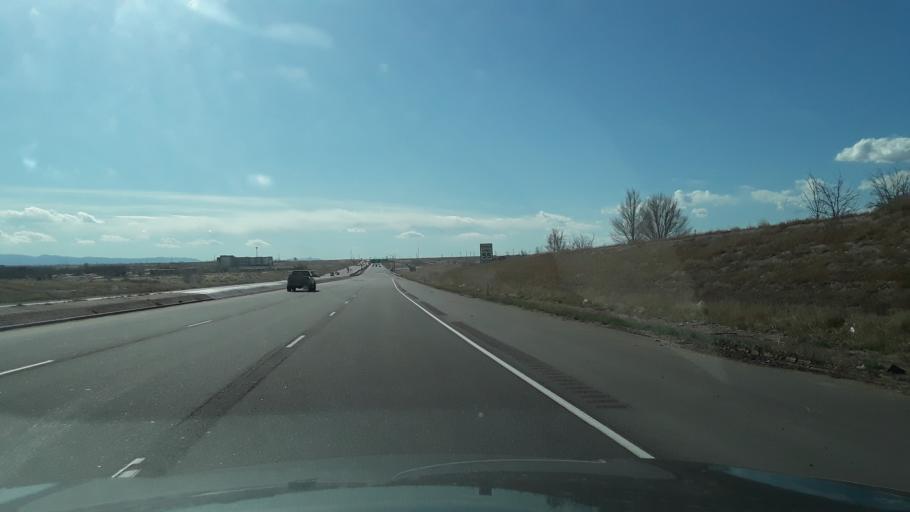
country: US
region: Colorado
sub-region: Pueblo County
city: Pueblo
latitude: 38.3122
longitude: -104.6478
